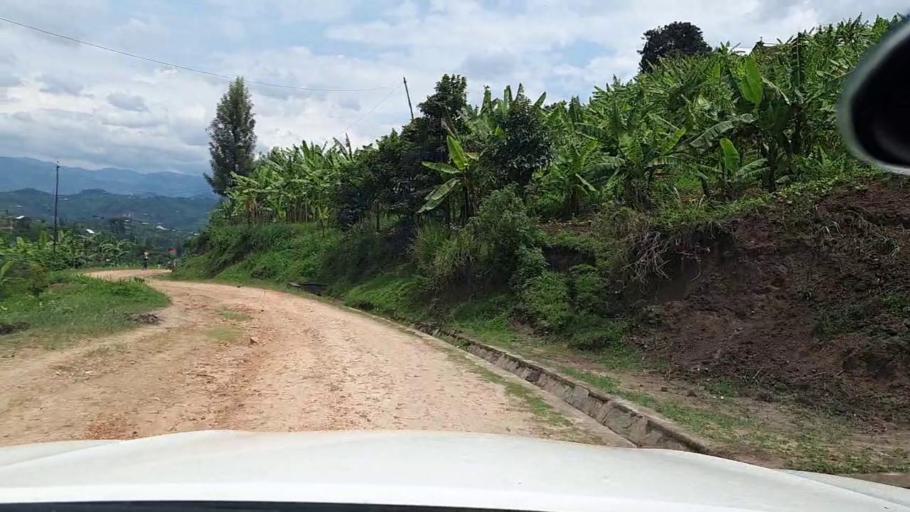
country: RW
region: Western Province
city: Kibuye
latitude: -2.0835
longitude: 29.4176
